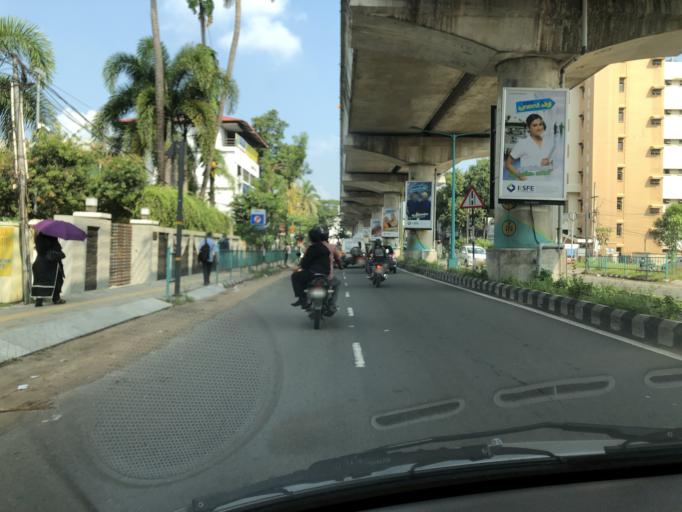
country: IN
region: Kerala
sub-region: Ernakulam
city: Elur
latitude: 10.0120
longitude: 76.3030
